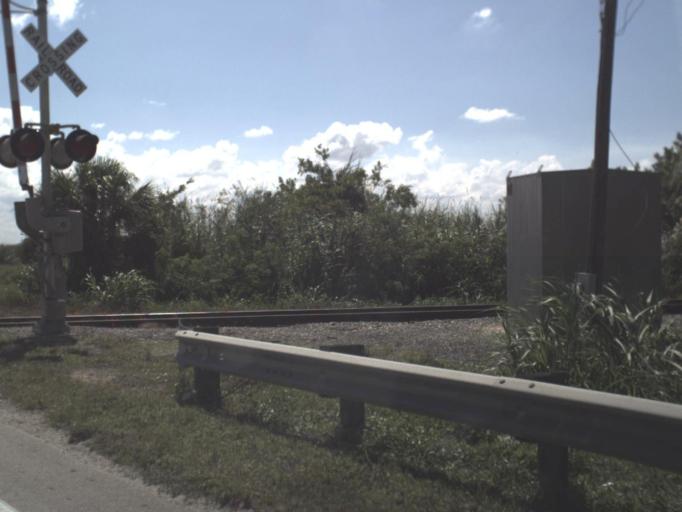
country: US
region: Florida
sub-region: Glades County
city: Moore Haven
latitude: 26.8520
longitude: -81.1228
